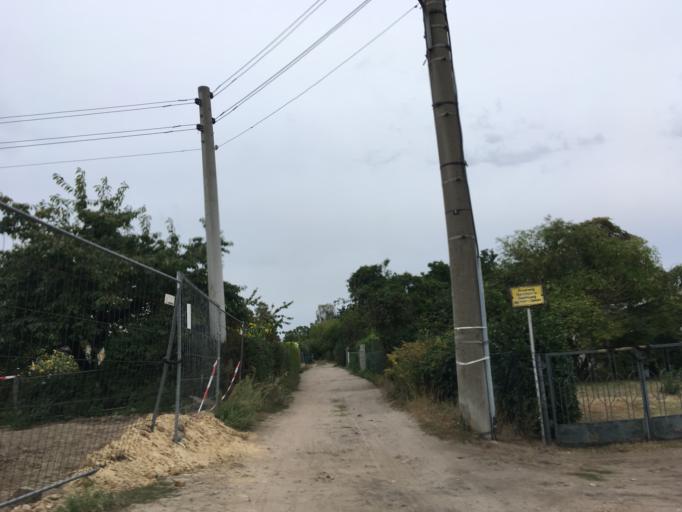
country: DE
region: Berlin
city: Niederschonhausen
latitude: 52.5939
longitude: 13.4154
